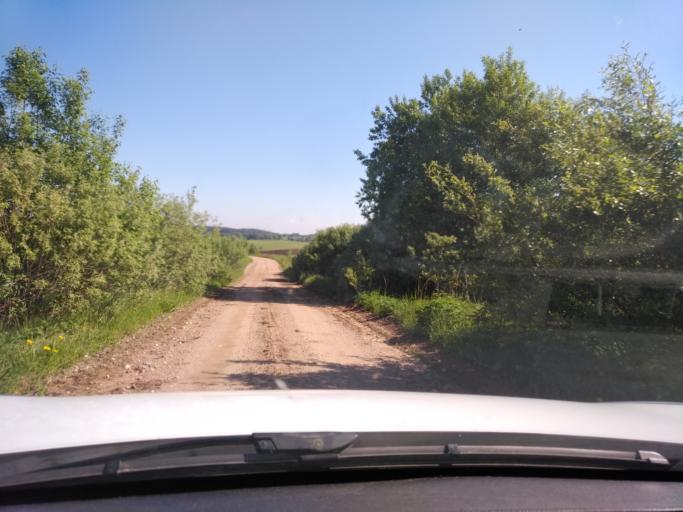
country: LT
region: Panevezys
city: Rokiskis
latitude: 55.7494
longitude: 25.6090
